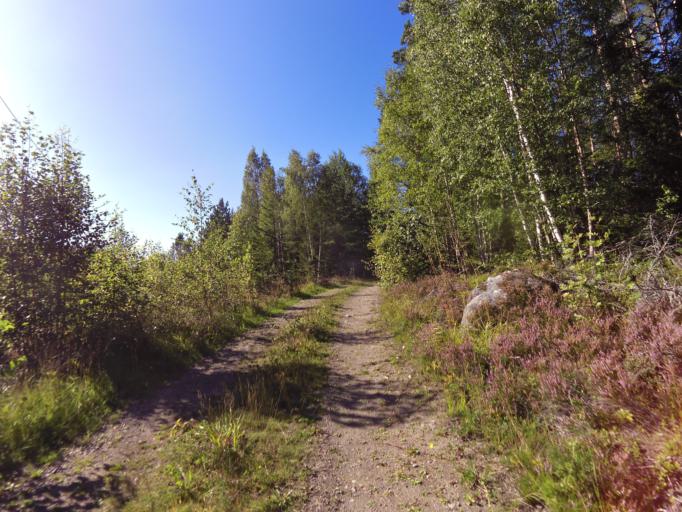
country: SE
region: Gaevleborg
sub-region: Hofors Kommun
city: Hofors
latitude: 60.5670
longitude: 16.4689
